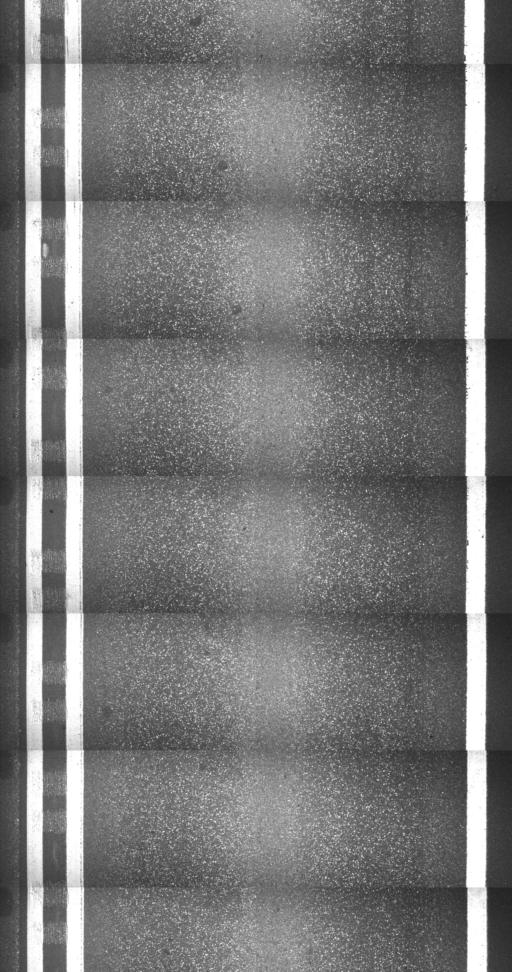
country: US
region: Vermont
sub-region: Washington County
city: Montpelier
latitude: 44.2279
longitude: -72.5568
